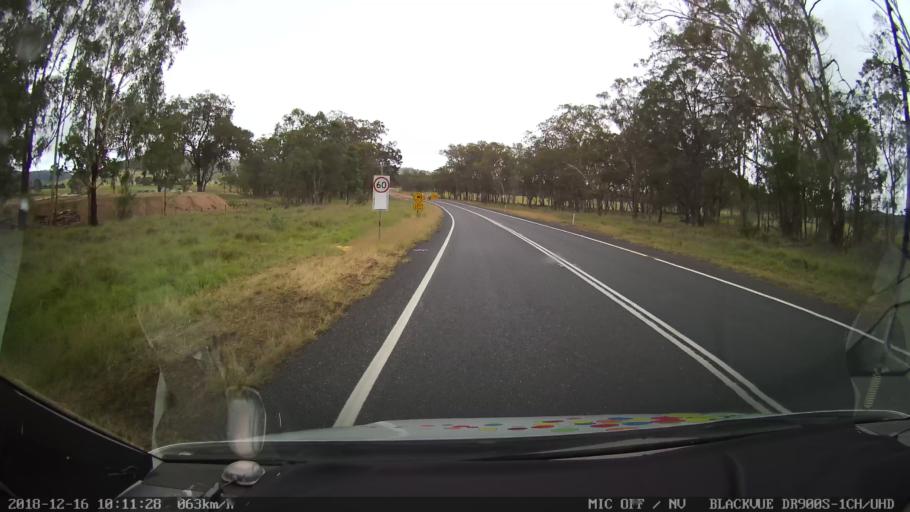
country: AU
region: New South Wales
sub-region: Glen Innes Severn
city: Glen Innes
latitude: -29.3130
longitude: 151.9329
